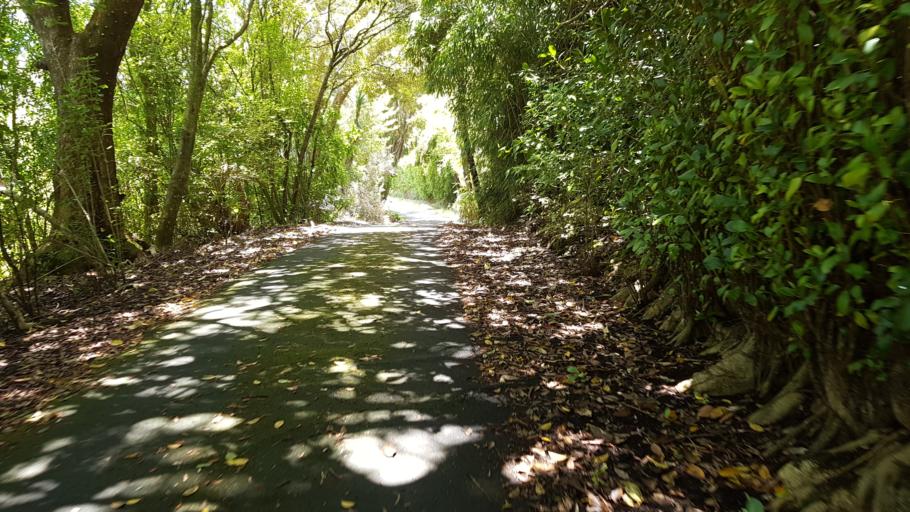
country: NZ
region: Auckland
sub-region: Auckland
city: North Shore
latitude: -36.8222
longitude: 174.7185
